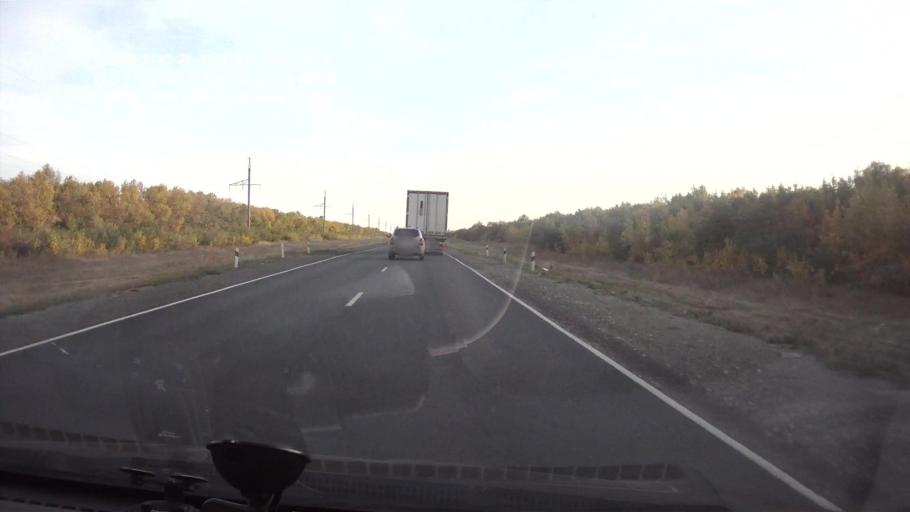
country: RU
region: Saratov
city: Krasnoarmeysk
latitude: 51.1367
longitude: 45.6502
